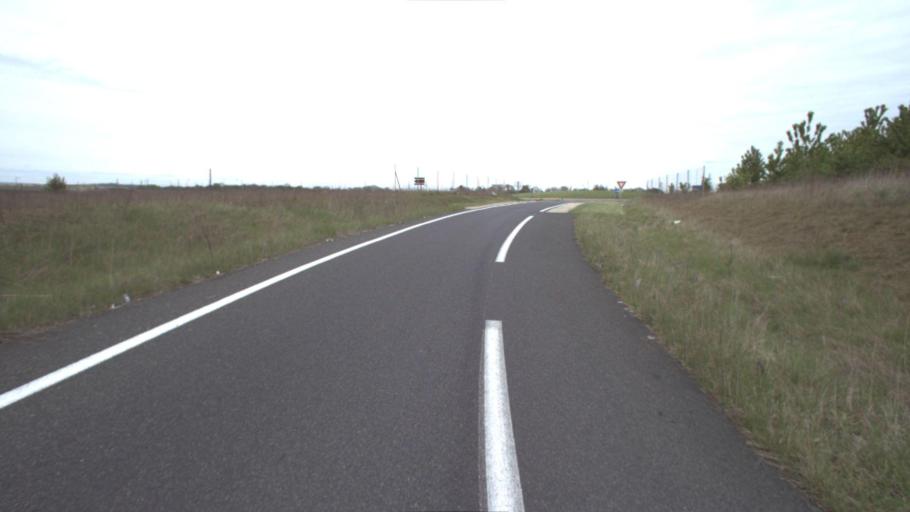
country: FR
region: Ile-de-France
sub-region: Departement de Seine-et-Marne
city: Villenoy
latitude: 48.9388
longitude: 2.8476
